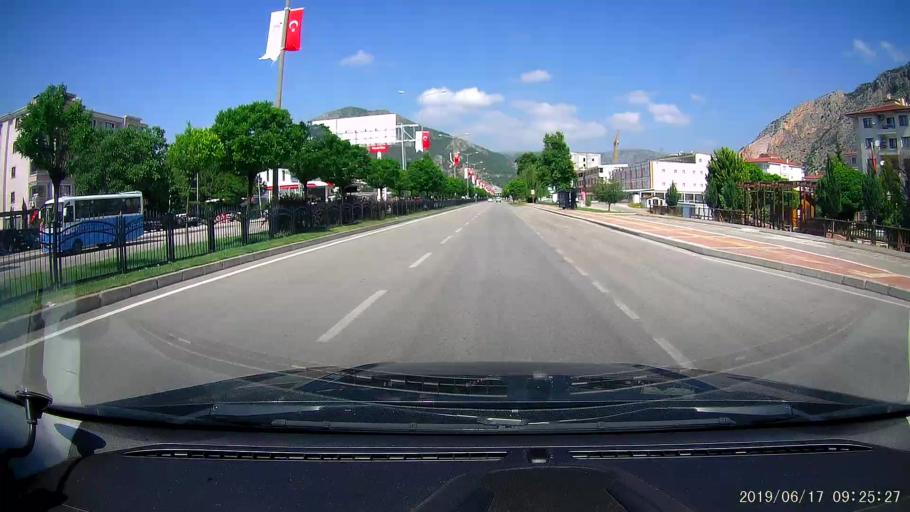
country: TR
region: Amasya
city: Amasya
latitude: 40.6677
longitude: 35.8485
